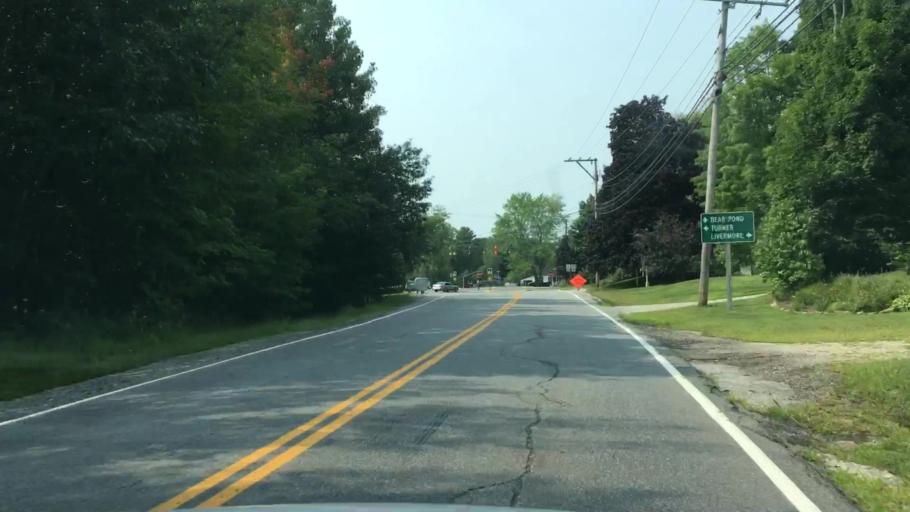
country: US
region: Maine
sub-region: Androscoggin County
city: Livermore
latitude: 44.3420
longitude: -70.2551
